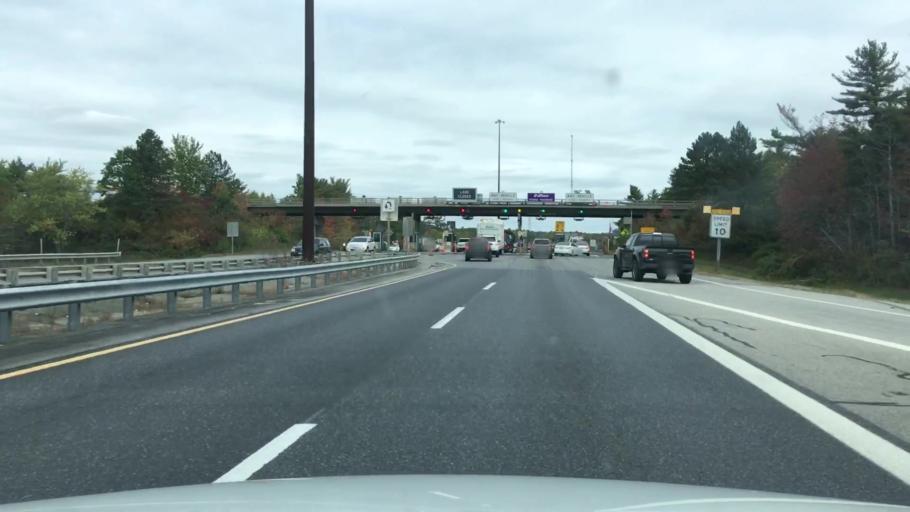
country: US
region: Maine
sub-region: Kennebec County
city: Gardiner
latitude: 44.2116
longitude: -69.8243
